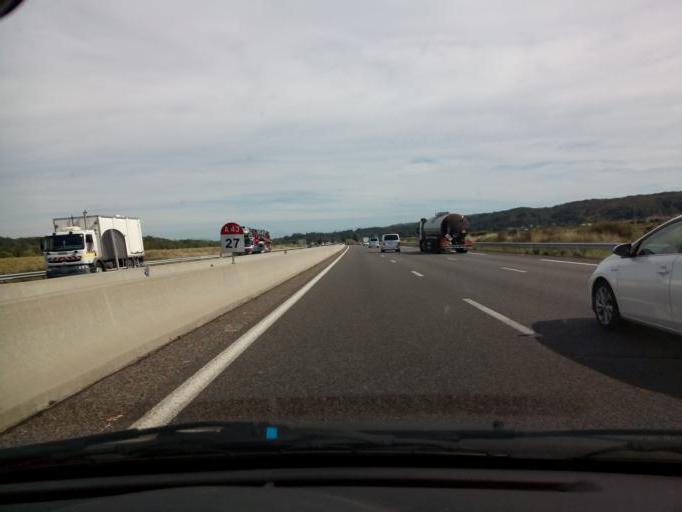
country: FR
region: Rhone-Alpes
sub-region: Departement de l'Isere
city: Vaulx-Milieu
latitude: 45.6209
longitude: 5.1838
